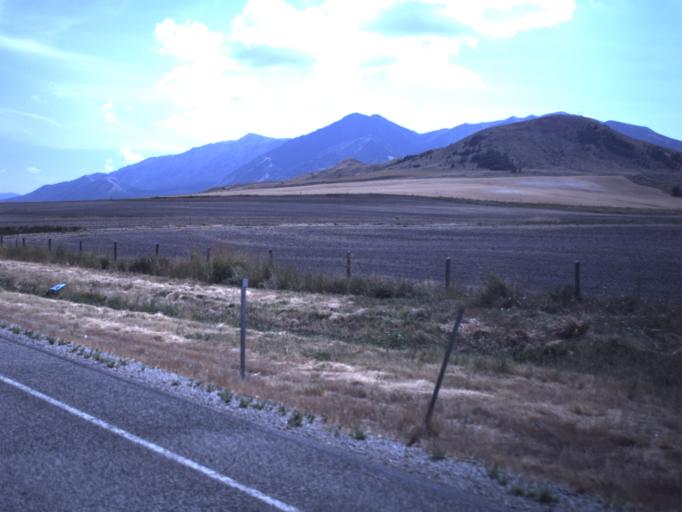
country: US
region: Utah
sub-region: Cache County
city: Mendon
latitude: 41.7715
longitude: -112.0164
